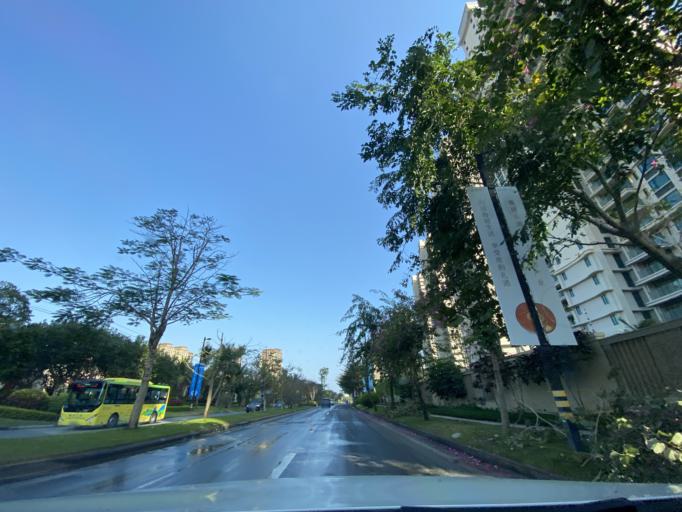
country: CN
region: Hainan
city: Xincun
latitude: 18.4238
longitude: 109.9354
